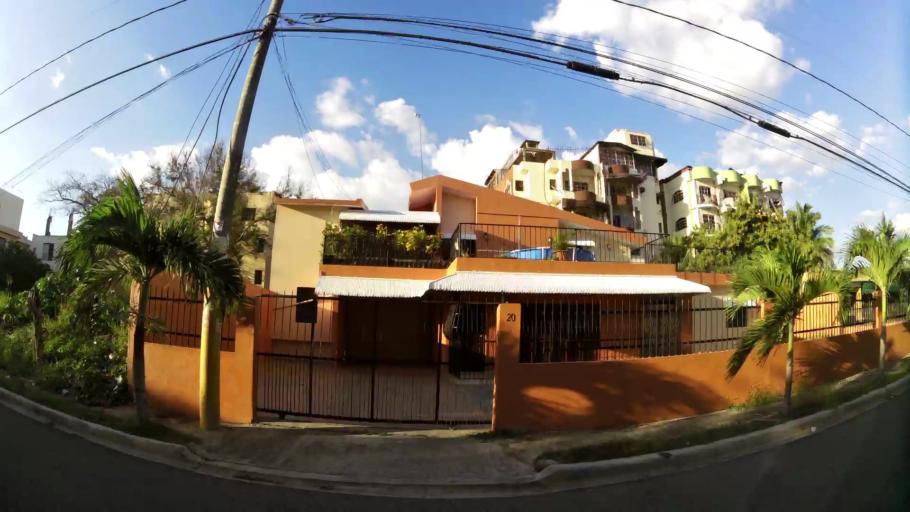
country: DO
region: Santo Domingo
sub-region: Santo Domingo
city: Santo Domingo Este
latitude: 18.4778
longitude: -69.8313
